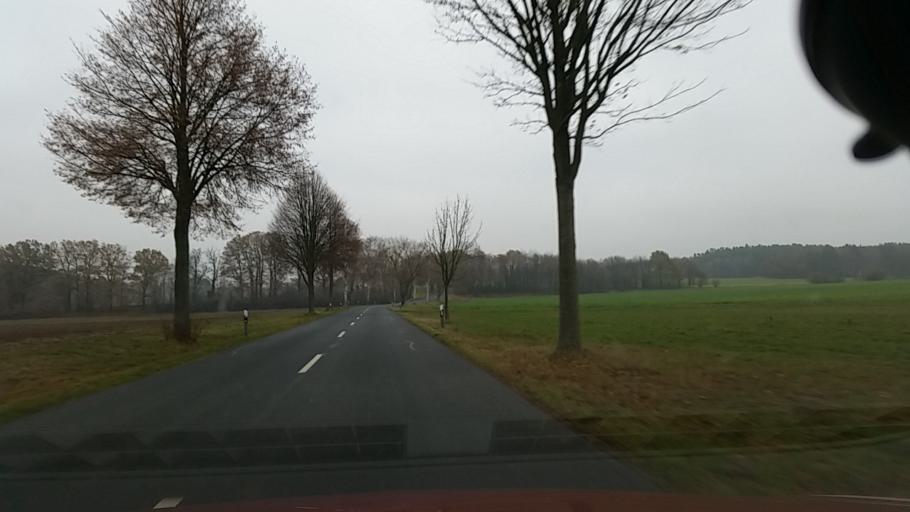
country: DE
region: Lower Saxony
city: Stadensen
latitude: 52.8525
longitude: 10.5670
